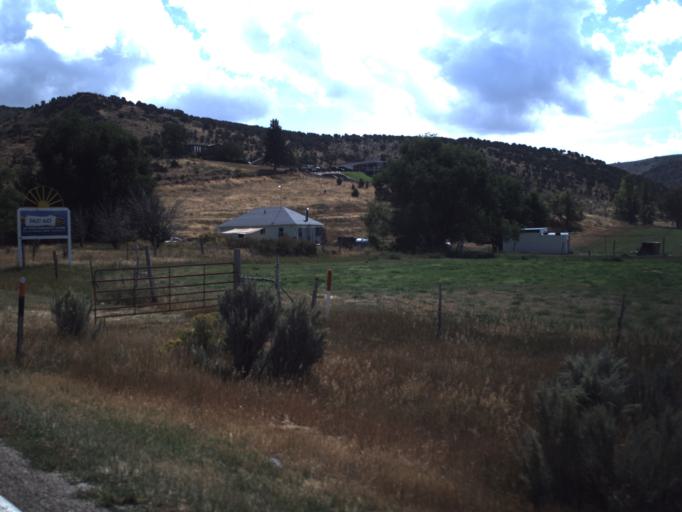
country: US
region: Utah
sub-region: Rich County
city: Randolph
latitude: 41.8287
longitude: -111.3158
